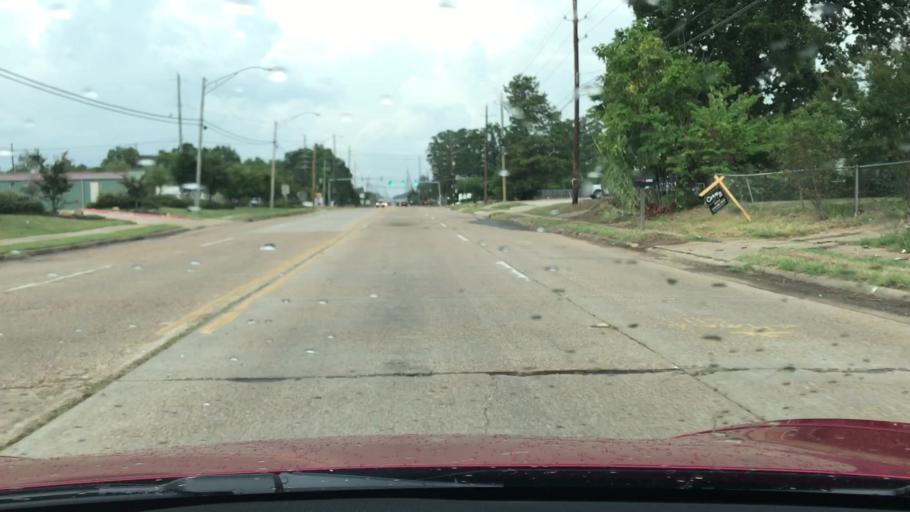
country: US
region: Louisiana
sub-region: Bossier Parish
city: Bossier City
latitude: 32.4111
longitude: -93.7632
